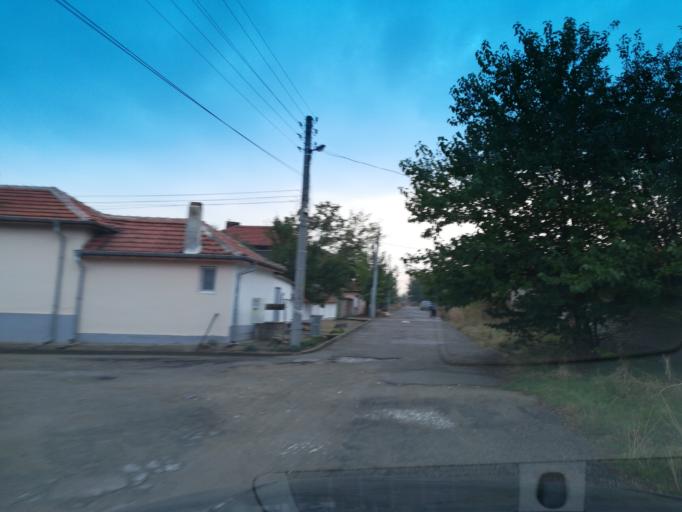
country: BG
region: Stara Zagora
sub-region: Obshtina Chirpan
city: Chirpan
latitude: 42.1740
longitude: 25.2076
